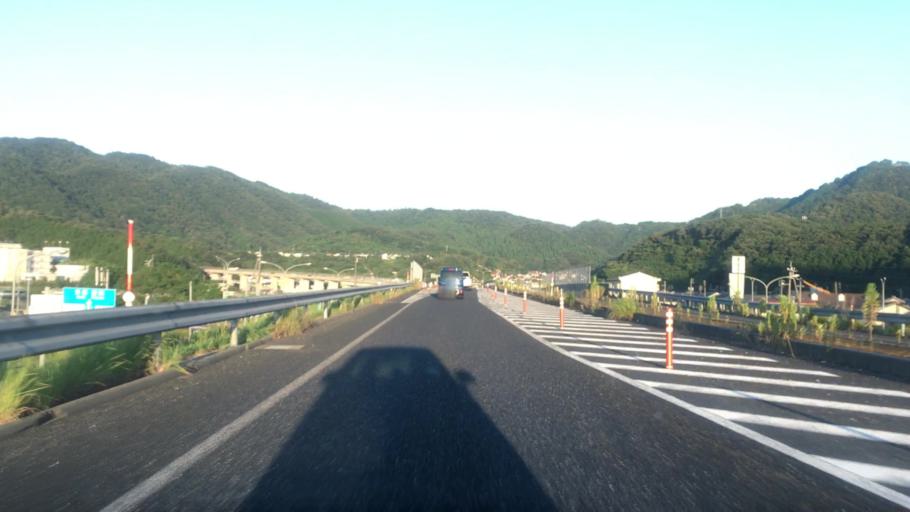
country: JP
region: Tottori
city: Tottori
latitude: 35.5233
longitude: 134.2277
